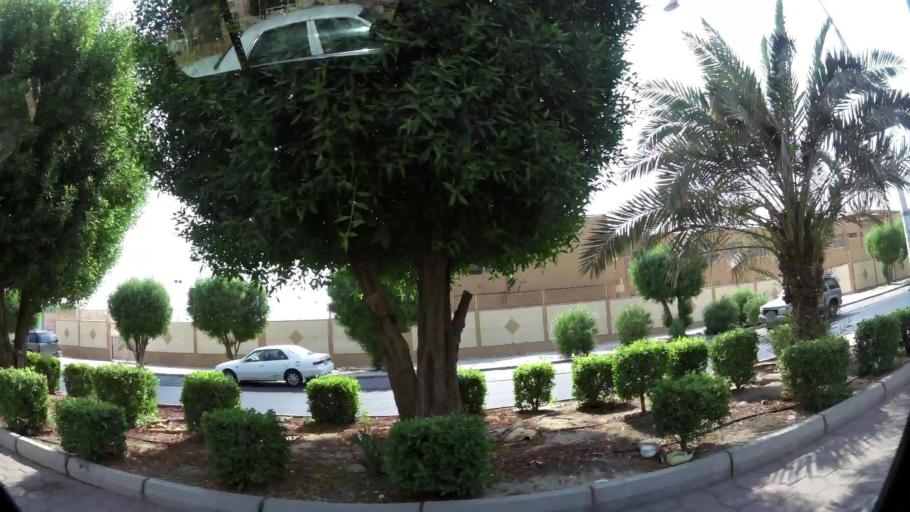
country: KW
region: Muhafazat al Jahra'
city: Al Jahra'
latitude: 29.3322
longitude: 47.6567
